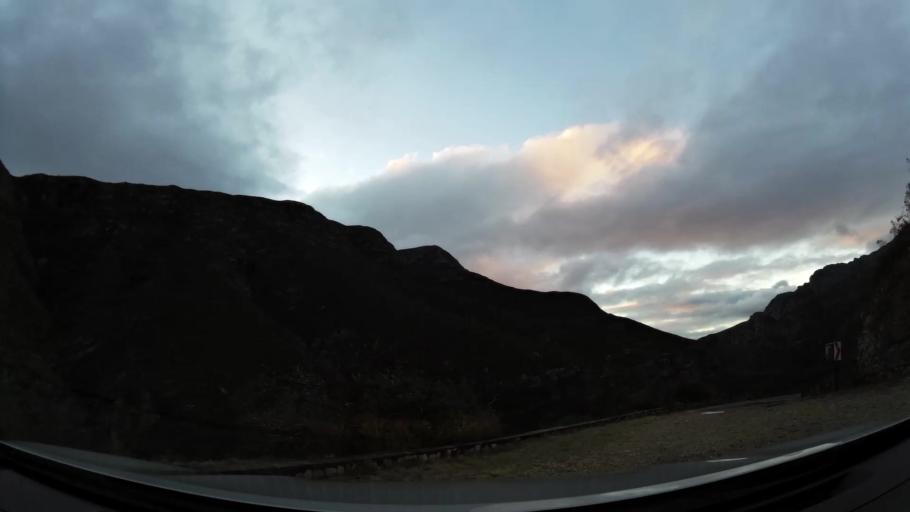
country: ZA
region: Western Cape
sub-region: Overberg District Municipality
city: Swellendam
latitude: -33.9741
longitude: 20.6993
